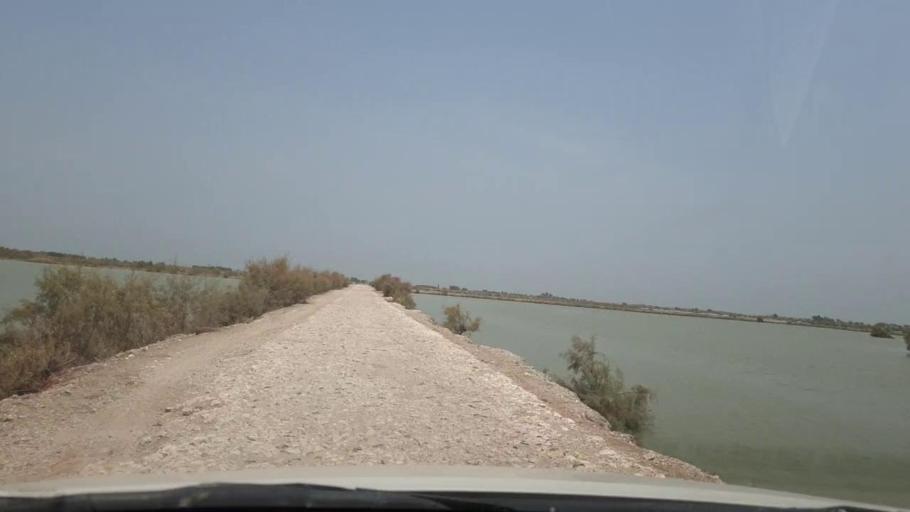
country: PK
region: Sindh
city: Rustam jo Goth
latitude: 28.0641
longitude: 68.8169
